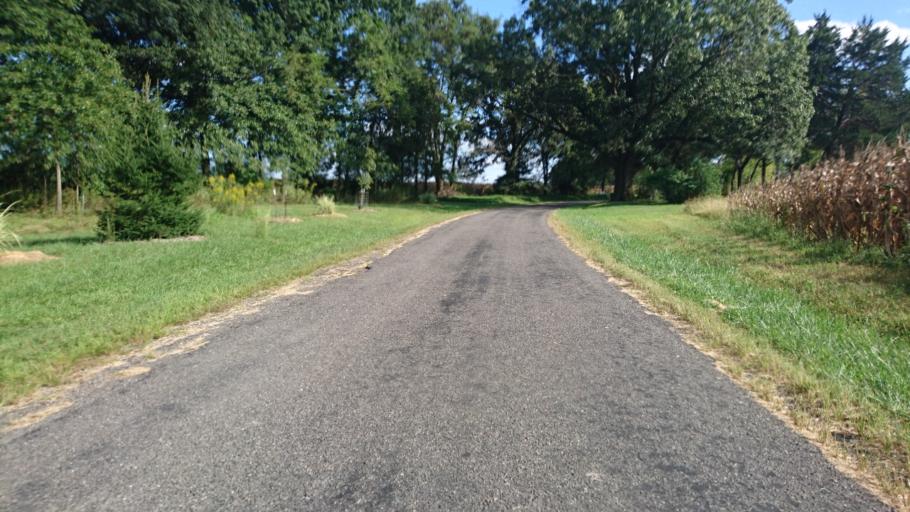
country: US
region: Illinois
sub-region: Macoupin County
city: Staunton
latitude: 38.9850
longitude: -89.7084
